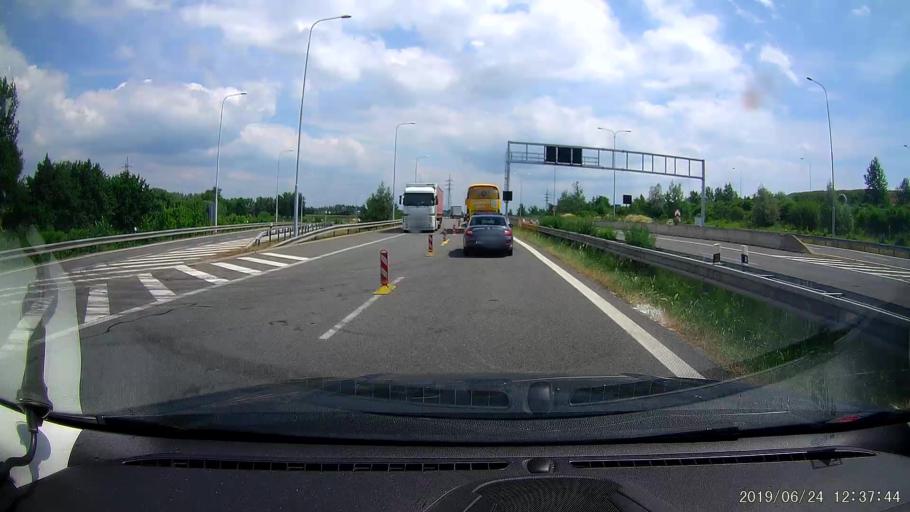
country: CZ
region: Moravskoslezsky
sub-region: Okres Ostrava-Mesto
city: Ostrava
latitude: 49.8745
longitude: 18.2986
